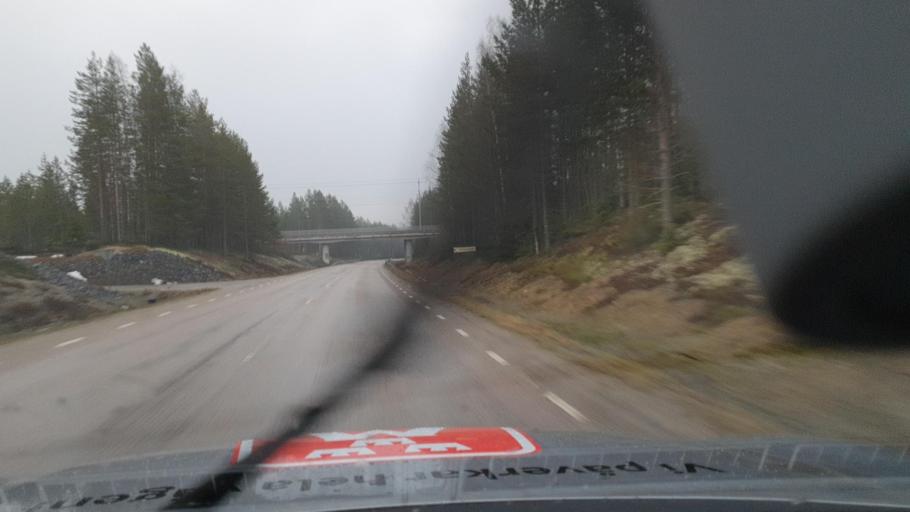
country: SE
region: Vaesternorrland
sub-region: OErnskoeldsviks Kommun
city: Bjasta
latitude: 63.2186
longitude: 18.4740
